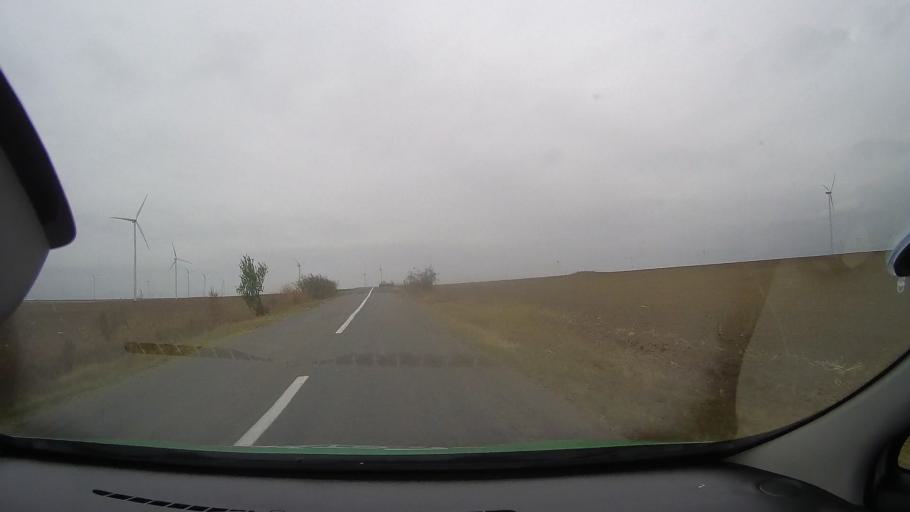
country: RO
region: Constanta
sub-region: Comuna Pantelimon
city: Pantelimon
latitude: 44.5084
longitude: 28.3423
